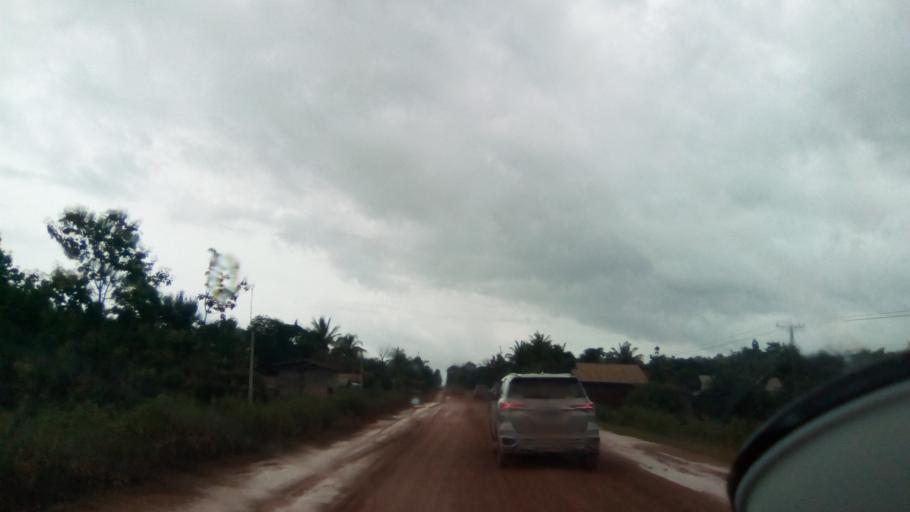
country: LA
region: Attapu
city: Attapu
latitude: 14.7491
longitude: 106.7000
